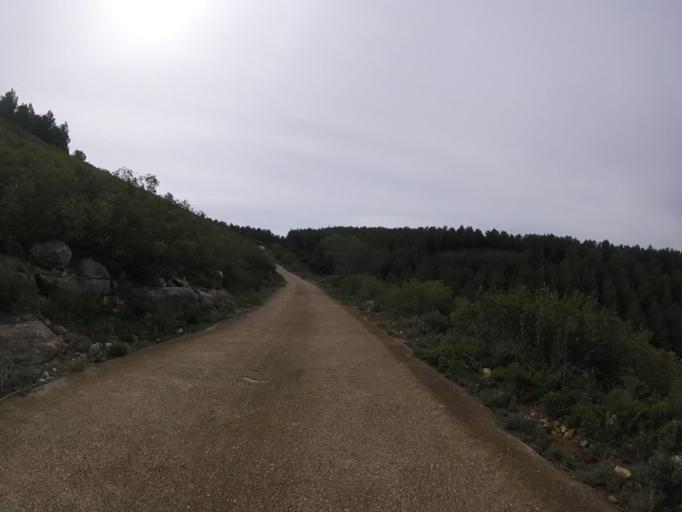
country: ES
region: Valencia
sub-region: Provincia de Castello
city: Cabanes
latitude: 40.1904
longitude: 0.0787
